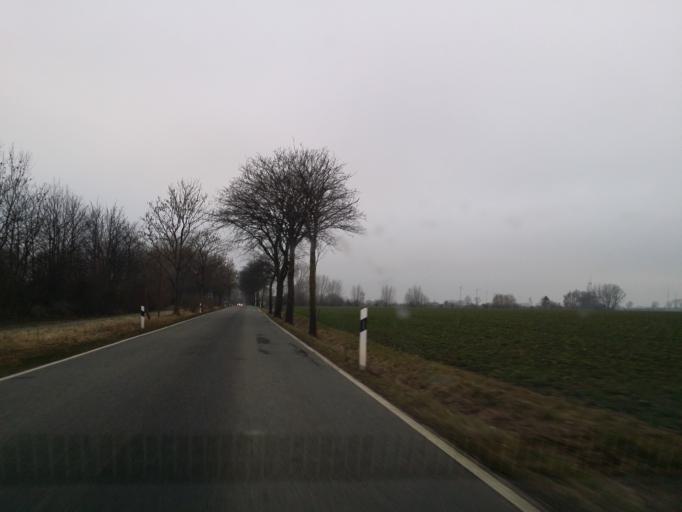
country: DE
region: Schleswig-Holstein
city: Fehmarn
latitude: 54.4606
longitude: 11.1235
